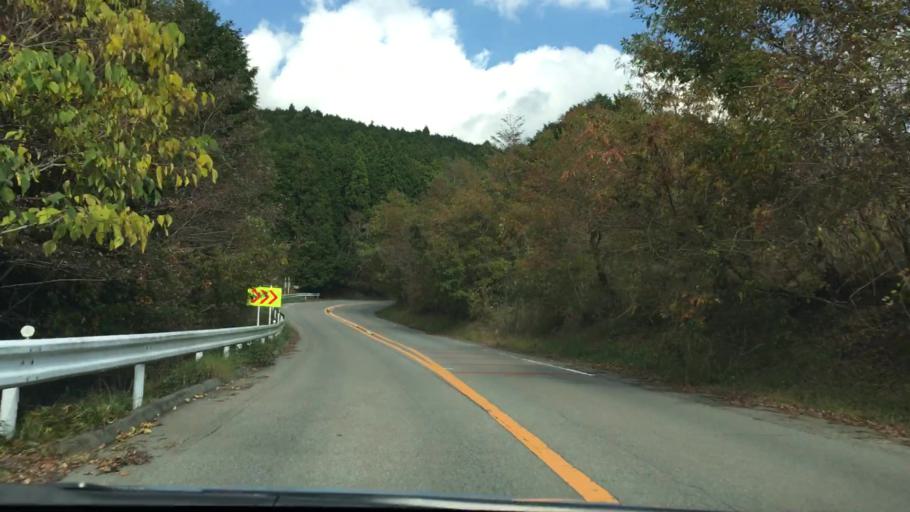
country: JP
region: Shizuoka
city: Gotemba
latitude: 35.3851
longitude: 138.9440
